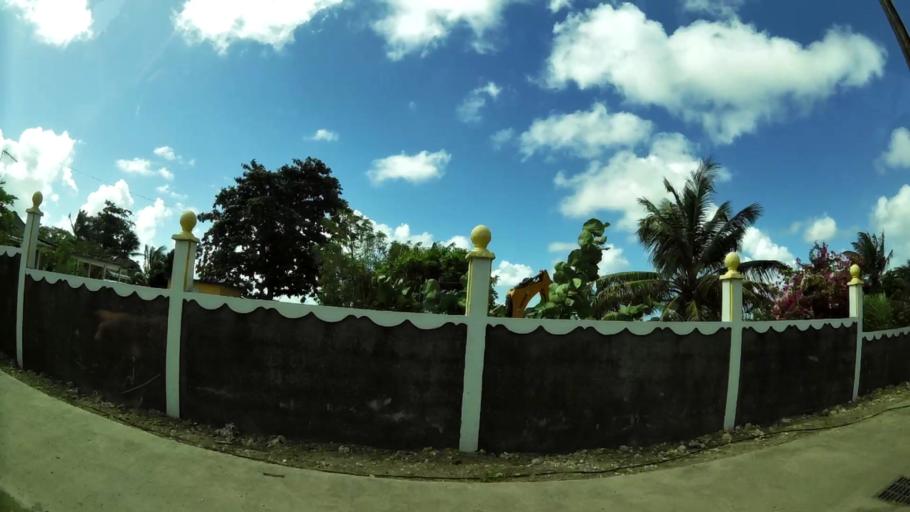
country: GP
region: Guadeloupe
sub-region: Guadeloupe
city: Petit-Canal
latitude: 16.4176
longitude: -61.4721
